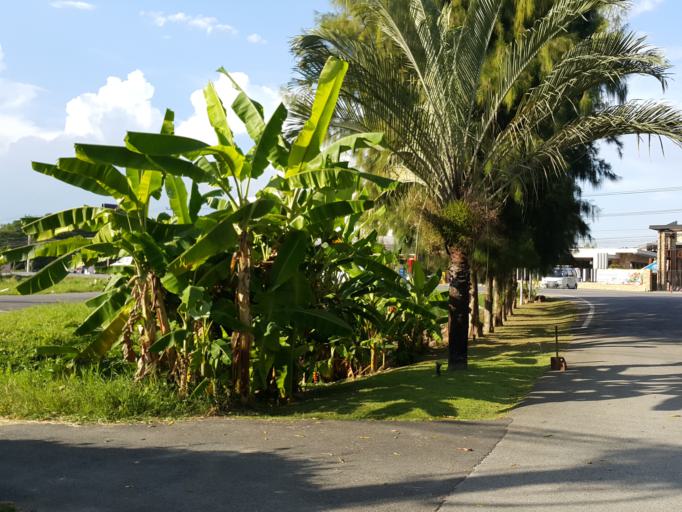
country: TH
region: Chiang Mai
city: Saraphi
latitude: 18.7560
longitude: 99.0513
